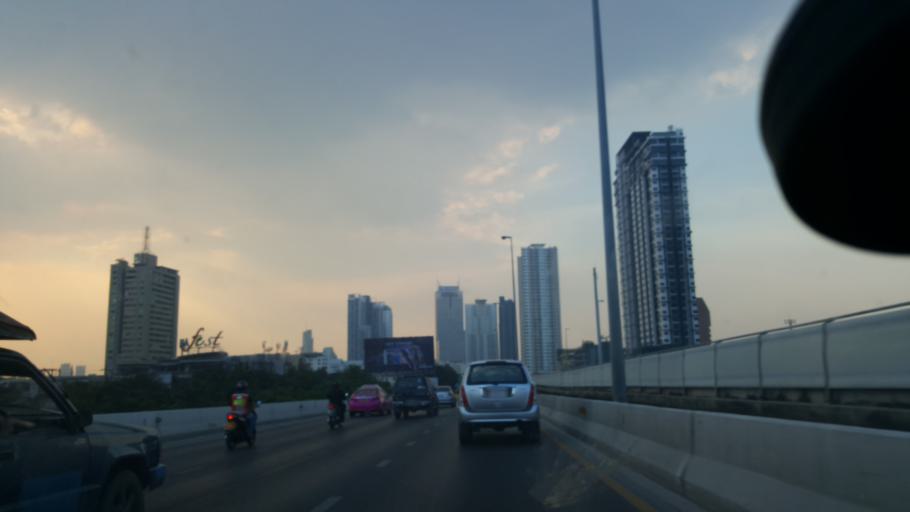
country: TH
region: Bangkok
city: Khlong San
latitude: 13.7197
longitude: 100.5101
